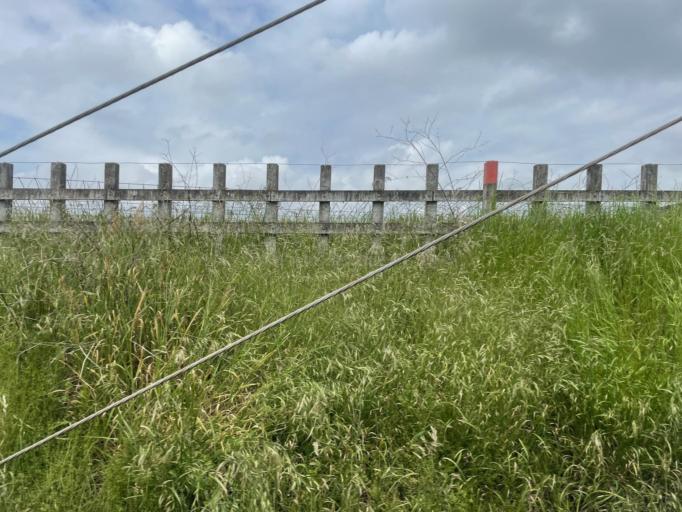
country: JP
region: Tochigi
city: Fujioka
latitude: 36.2837
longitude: 139.6612
